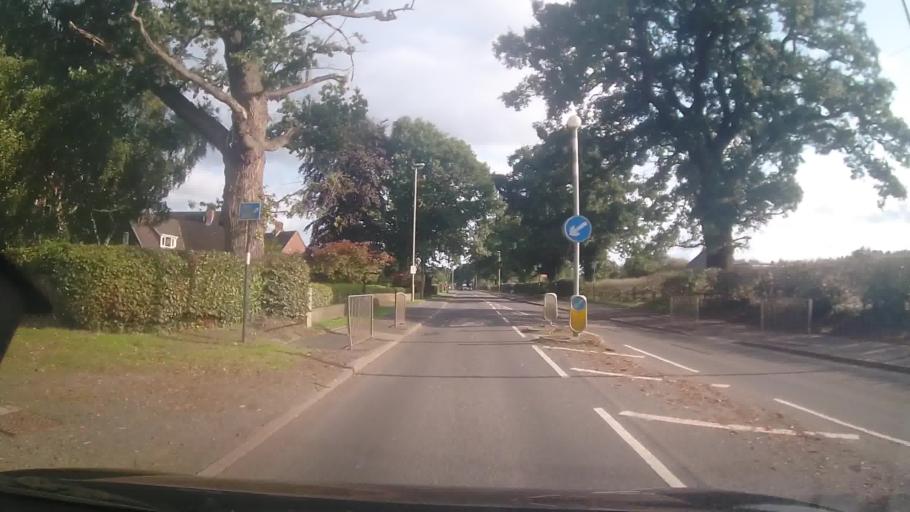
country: GB
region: England
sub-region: Shropshire
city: Ludlow
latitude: 52.3795
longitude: -2.7278
